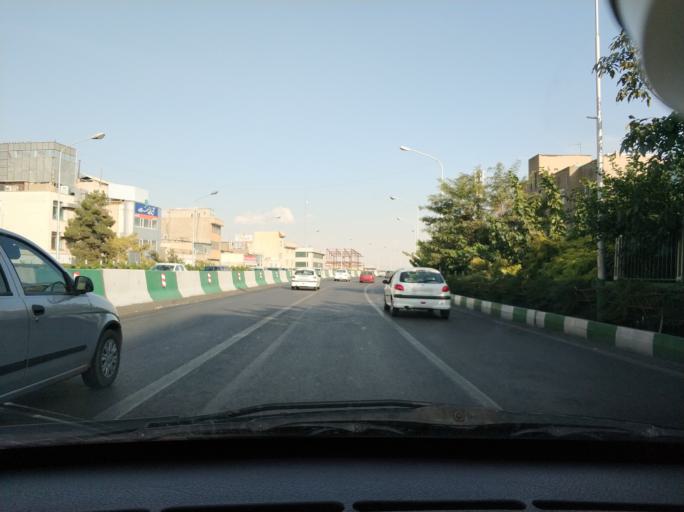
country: IR
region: Tehran
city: Tehran
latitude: 35.7426
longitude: 51.4431
